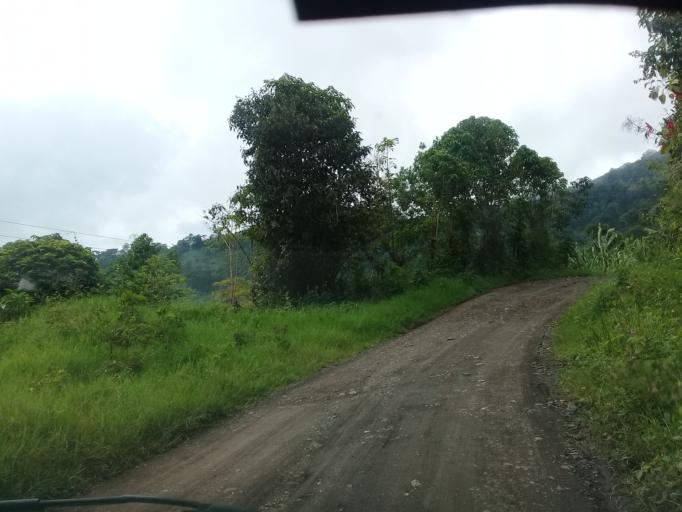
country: CO
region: Cundinamarca
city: Quipile
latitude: 4.7219
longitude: -74.5425
